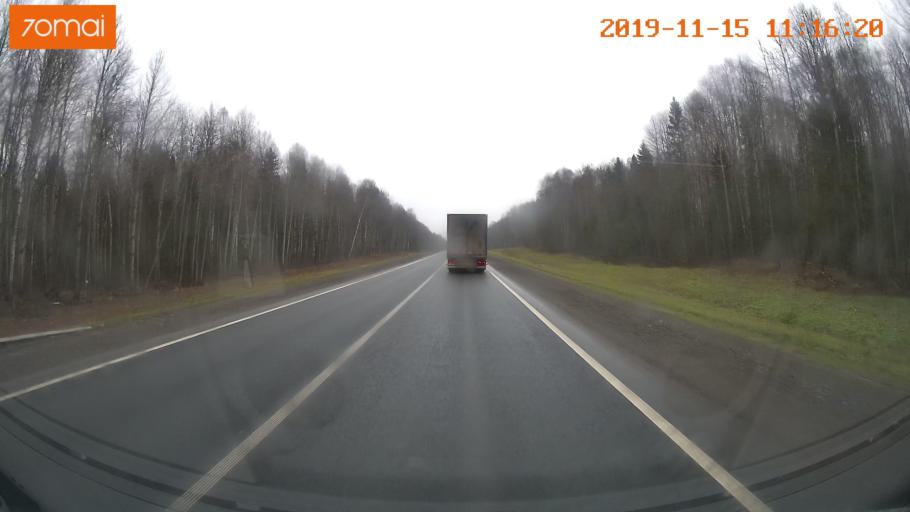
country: RU
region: Vologda
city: Chebsara
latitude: 59.1301
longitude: 39.2279
